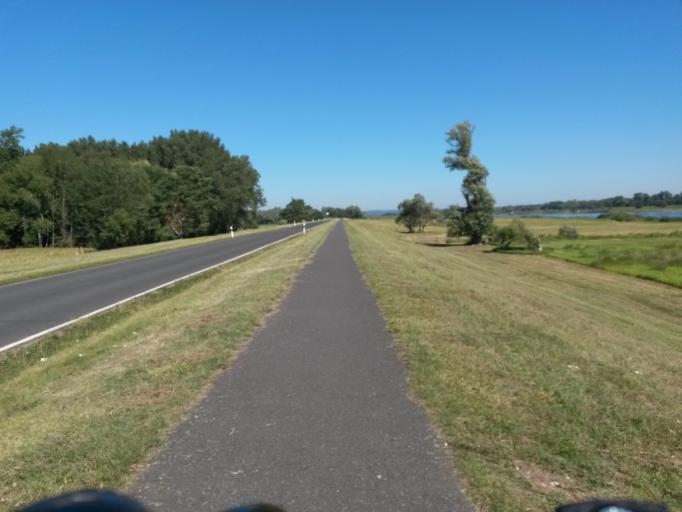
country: PL
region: West Pomeranian Voivodeship
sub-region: Powiat gryfinski
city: Cedynia
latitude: 52.8585
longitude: 14.1325
